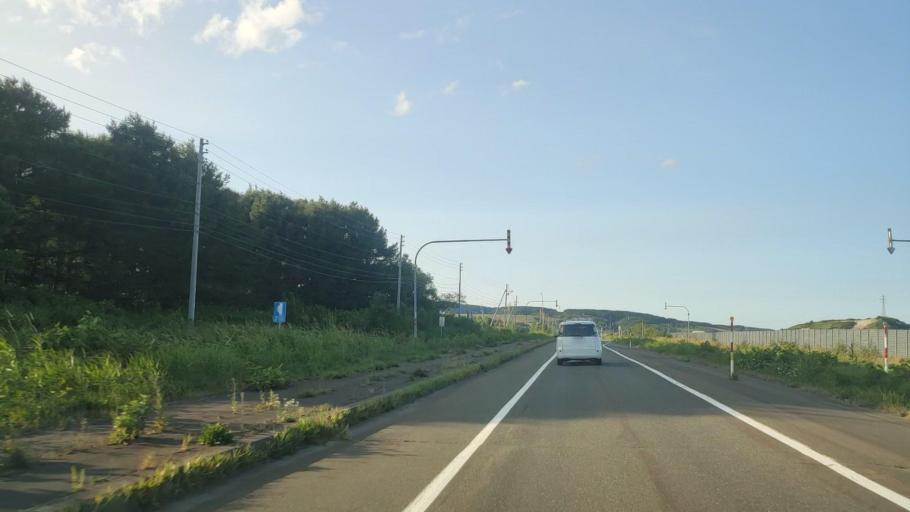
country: JP
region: Hokkaido
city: Wakkanai
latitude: 45.3249
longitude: 141.7196
